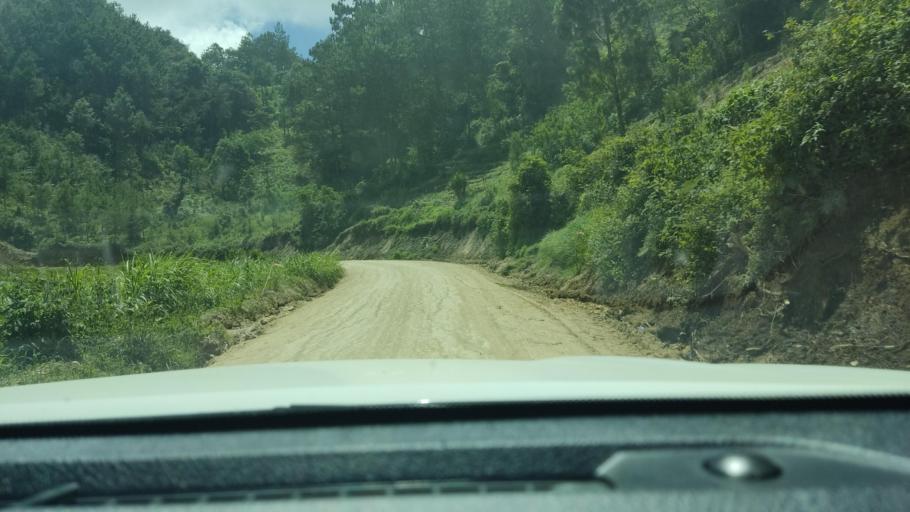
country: GT
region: Chimaltenango
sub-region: Municipio de San Juan Comalapa
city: Comalapa
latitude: 14.7713
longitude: -90.8789
